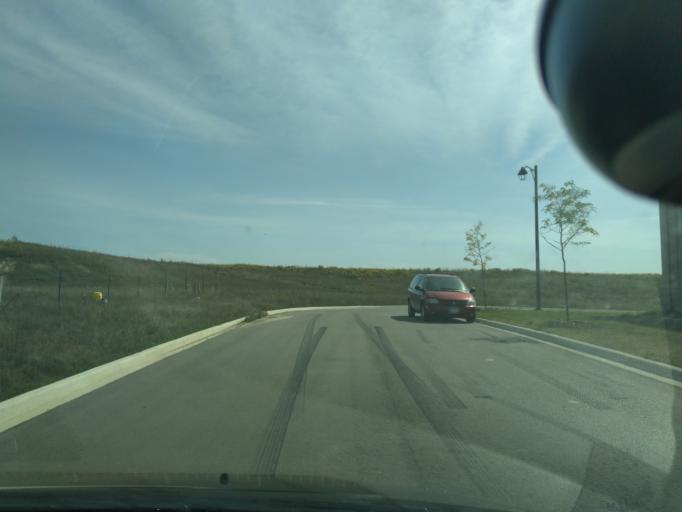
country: CA
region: Ontario
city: Newmarket
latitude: 44.0862
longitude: -79.4446
